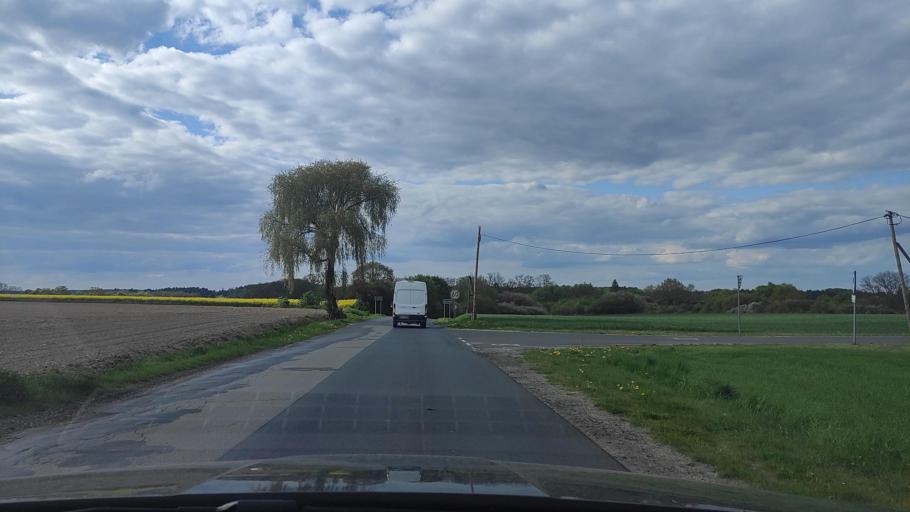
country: PL
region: Greater Poland Voivodeship
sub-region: Powiat poznanski
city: Kostrzyn
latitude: 52.4449
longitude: 17.1688
